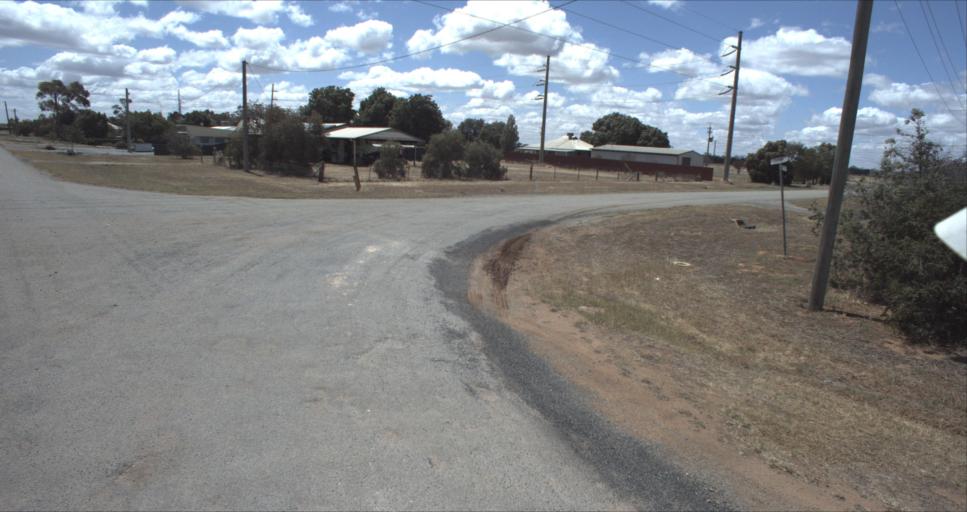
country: AU
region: New South Wales
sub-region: Murrumbidgee Shire
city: Darlington Point
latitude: -34.5123
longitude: 146.1845
